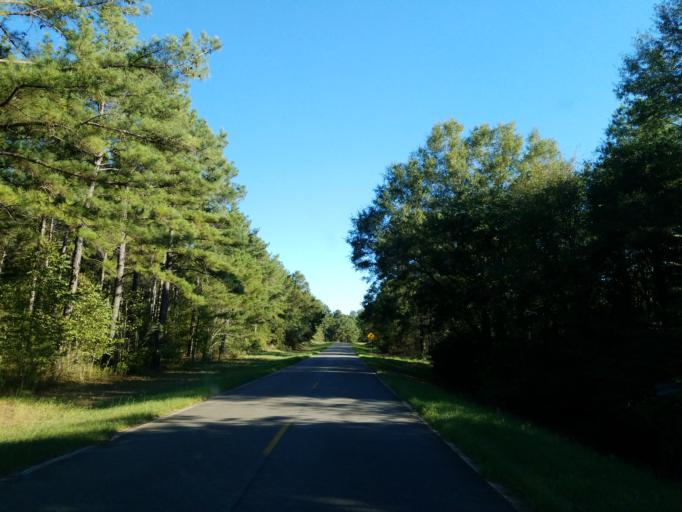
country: US
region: Georgia
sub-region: Lee County
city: Leesburg
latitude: 31.9097
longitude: -84.0366
